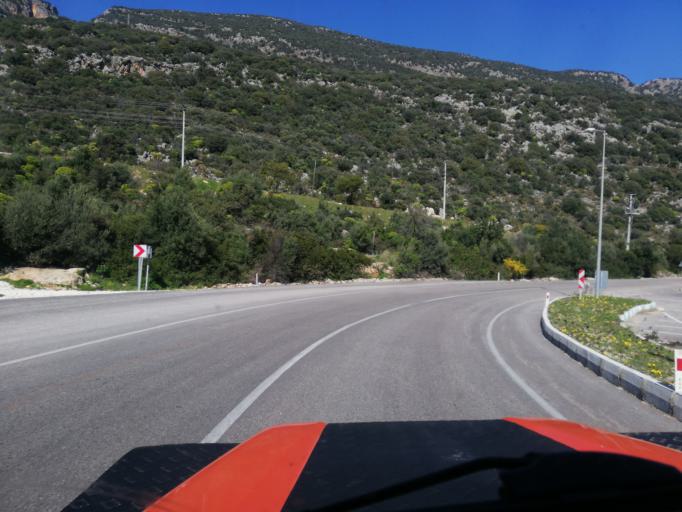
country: TR
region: Antalya
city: Kas
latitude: 36.2065
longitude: 29.5999
